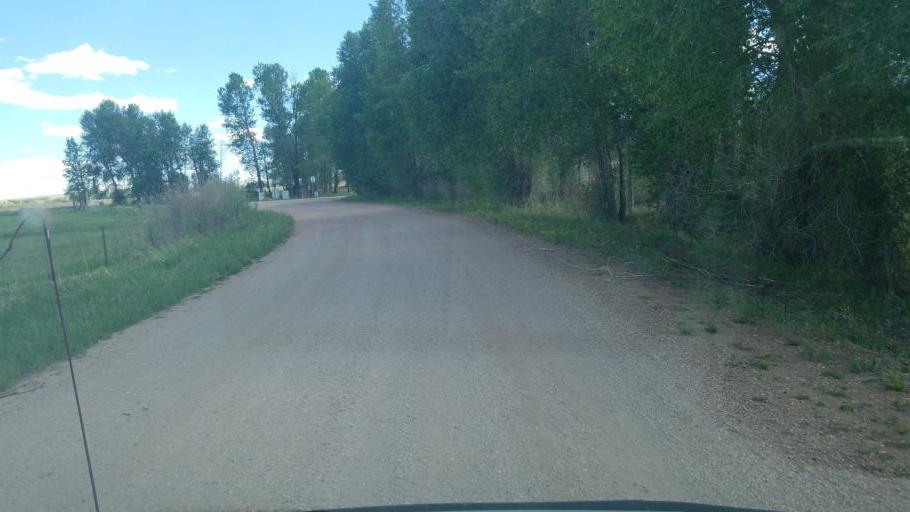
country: US
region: Colorado
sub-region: Custer County
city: Westcliffe
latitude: 38.2370
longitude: -105.5990
